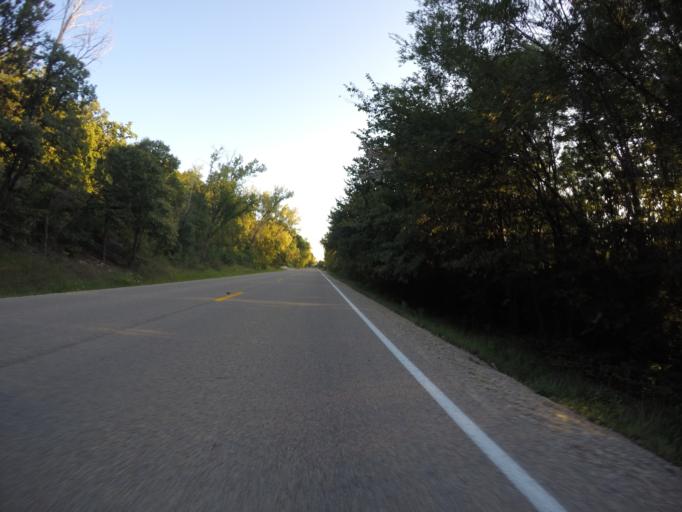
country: US
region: Kansas
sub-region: Riley County
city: Manhattan
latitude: 39.1639
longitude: -96.5552
